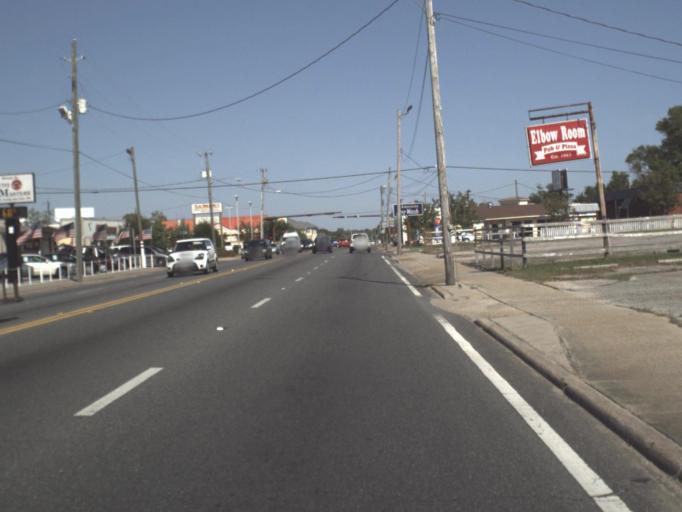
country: US
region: Florida
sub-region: Escambia County
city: Pensacola
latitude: 30.4207
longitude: -87.2432
